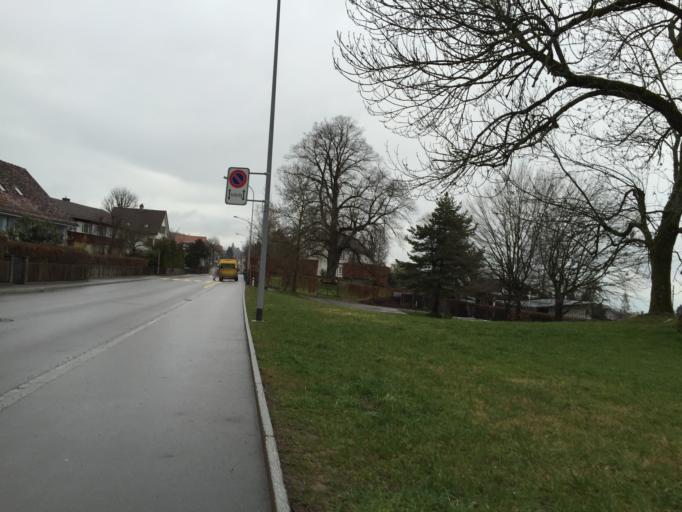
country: CH
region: Saint Gallen
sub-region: Wahlkreis St. Gallen
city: Sankt Gallen
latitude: 47.4335
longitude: 9.3745
